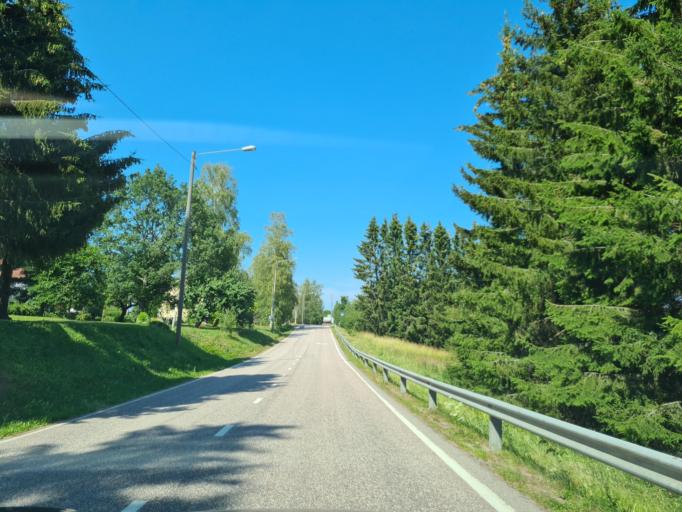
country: FI
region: Varsinais-Suomi
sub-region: Loimaa
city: Aura
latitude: 60.6410
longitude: 22.5916
